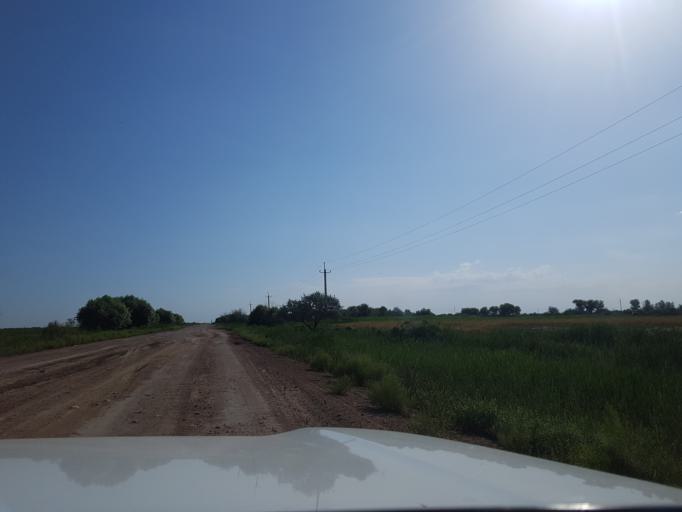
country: TM
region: Dasoguz
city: Koeneuergench
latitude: 42.0434
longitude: 58.8202
